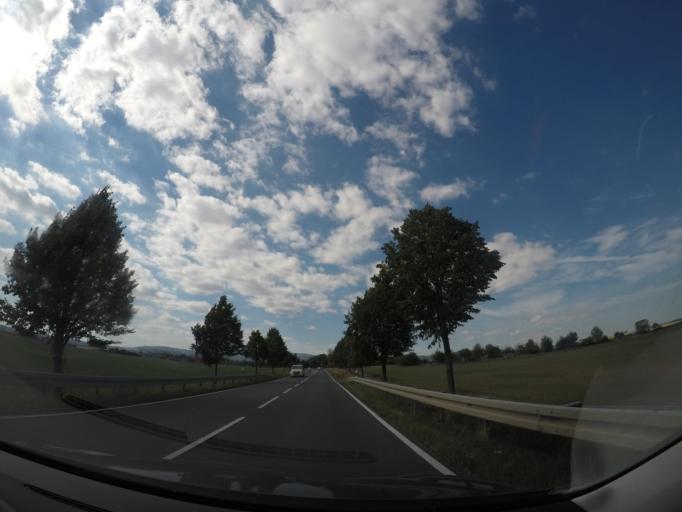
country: DE
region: Saxony-Anhalt
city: Wasserleben
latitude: 51.8995
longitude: 10.7706
